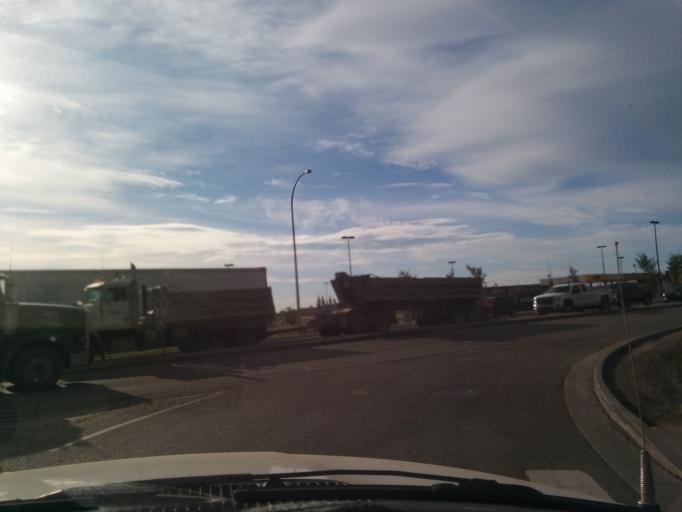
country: CA
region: Alberta
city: Grande Prairie
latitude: 55.1560
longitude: -118.8209
